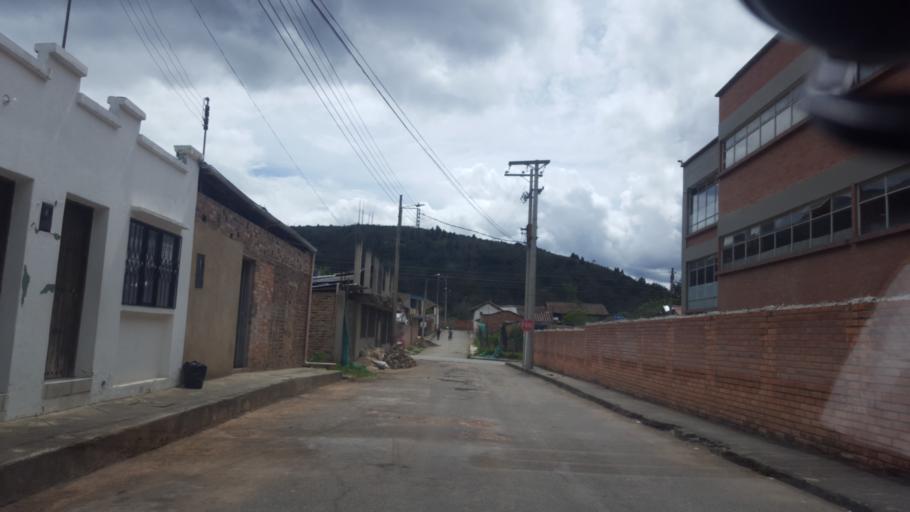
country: CO
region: Boyaca
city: Belen
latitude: 5.9922
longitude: -72.9147
